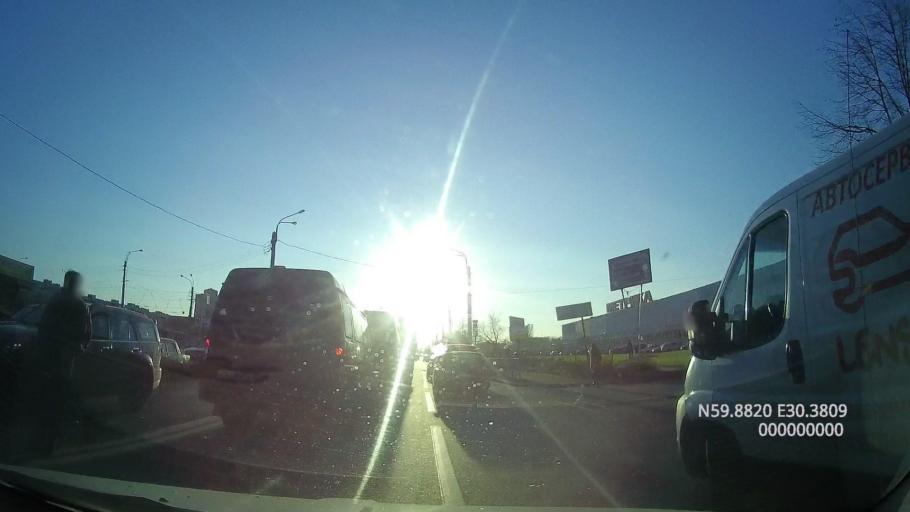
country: RU
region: St.-Petersburg
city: Kupchino
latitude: 59.8820
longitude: 30.3808
